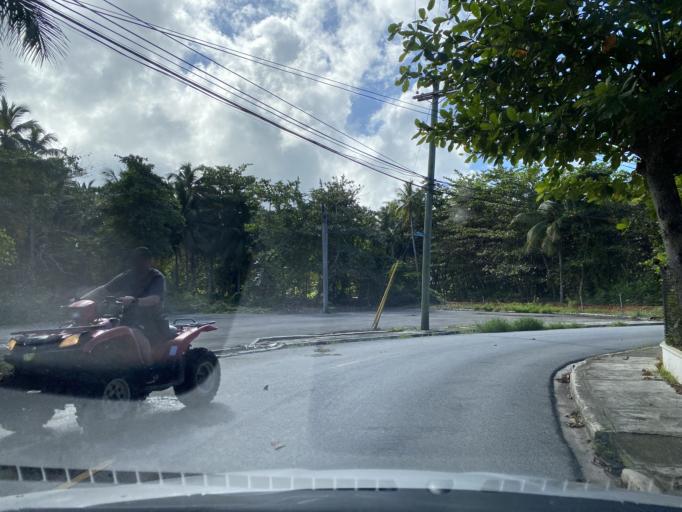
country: DO
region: Samana
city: Las Terrenas
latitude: 19.3106
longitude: -69.5692
